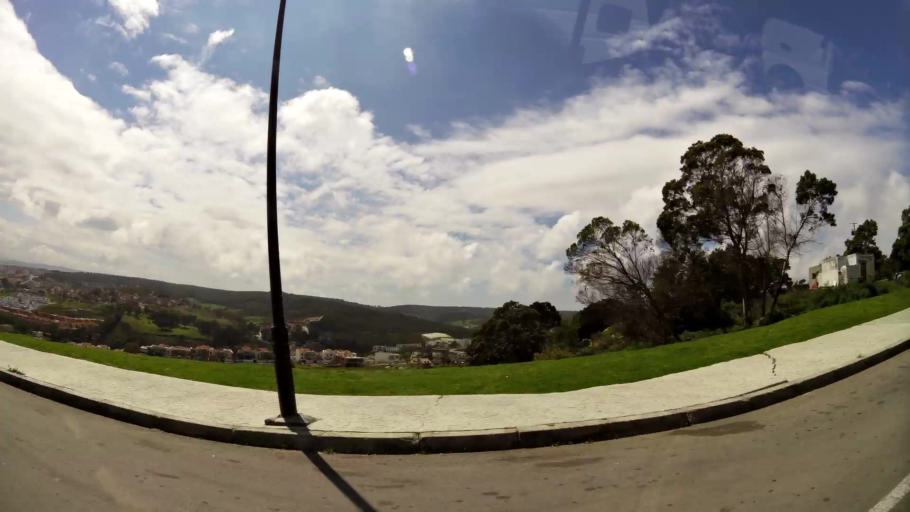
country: MA
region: Tanger-Tetouan
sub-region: Tanger-Assilah
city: Boukhalef
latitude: 35.7834
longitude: -5.8645
